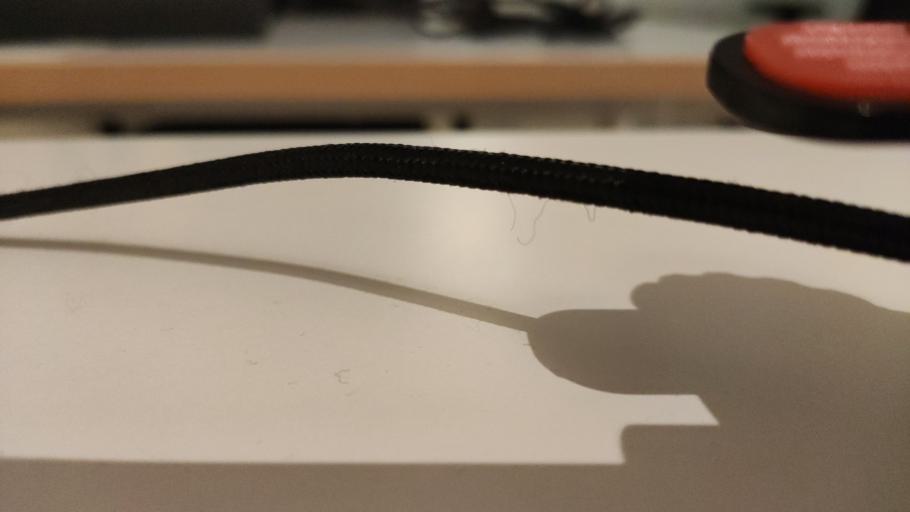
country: RU
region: Moskovskaya
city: Kurovskoye
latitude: 55.5836
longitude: 38.8904
